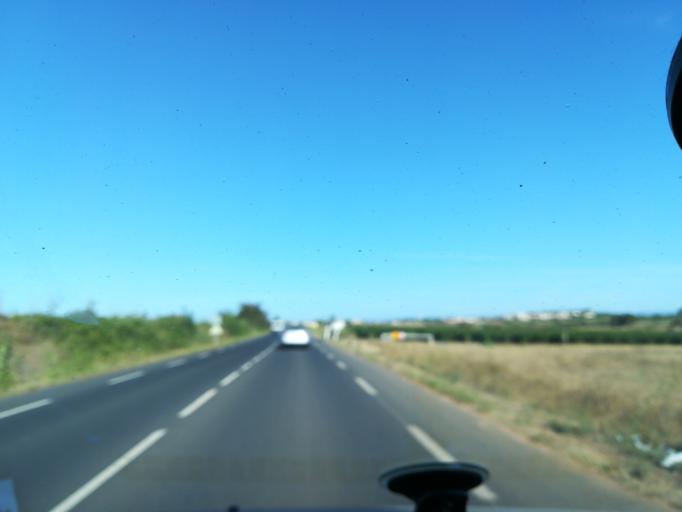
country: FR
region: Languedoc-Roussillon
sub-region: Departement de l'Herault
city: Portiragnes
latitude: 43.2941
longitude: 3.3580
